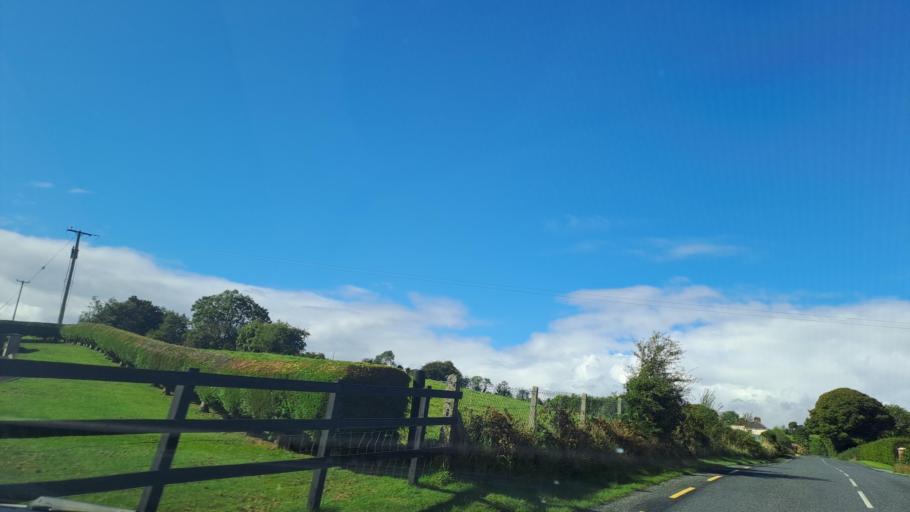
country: IE
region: Ulster
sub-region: An Cabhan
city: Kingscourt
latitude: 53.9445
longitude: -6.8361
